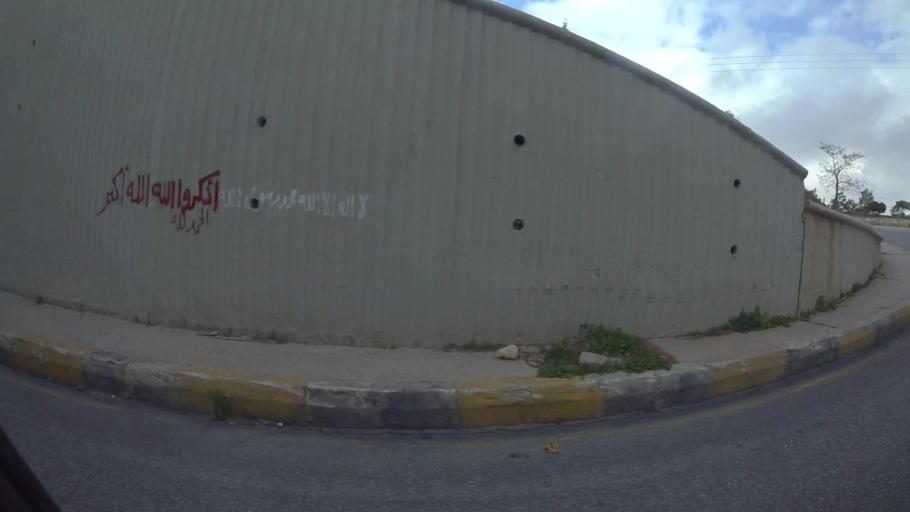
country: JO
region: Amman
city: Al Jubayhah
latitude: 32.0462
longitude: 35.8713
